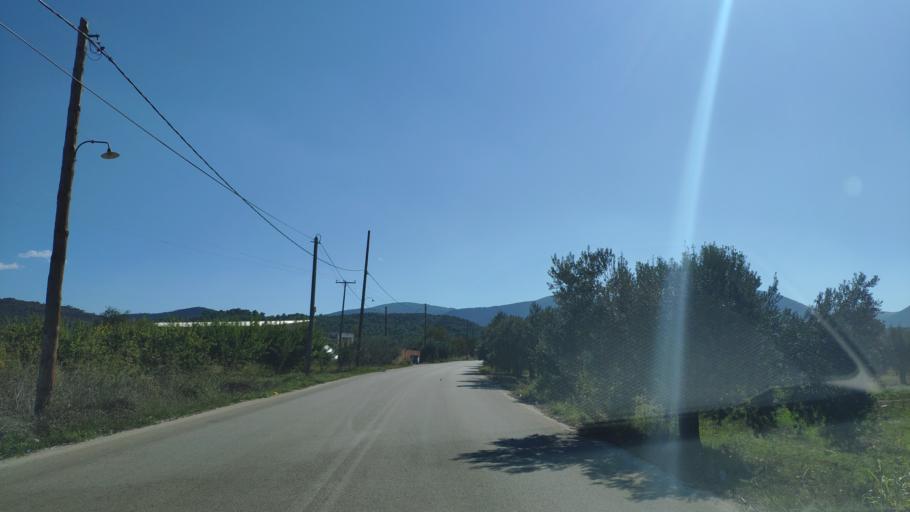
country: GR
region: Peloponnese
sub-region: Nomos Korinthias
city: Athikia
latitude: 37.8386
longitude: 22.9115
